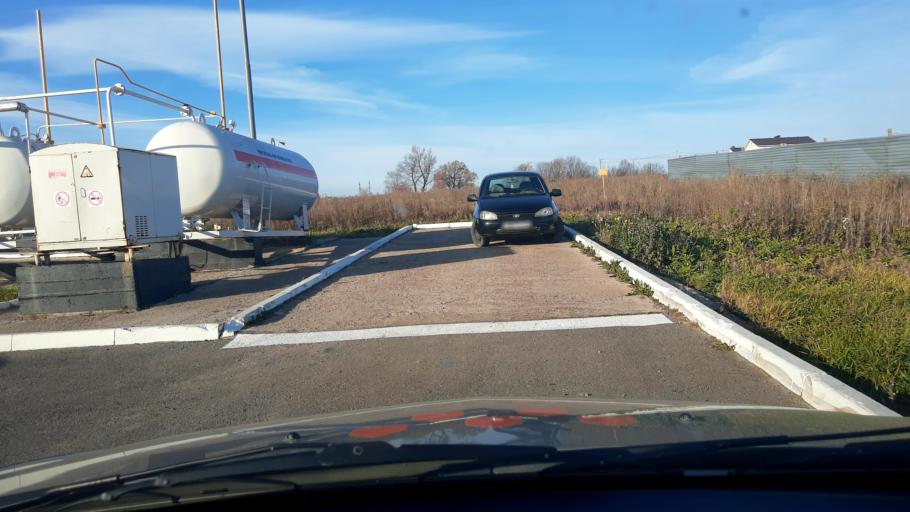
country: RU
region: Bashkortostan
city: Avdon
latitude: 54.7216
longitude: 55.8061
